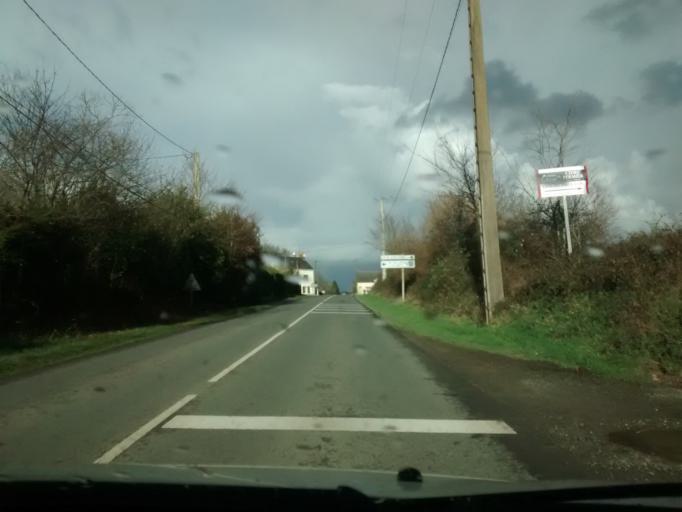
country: FR
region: Brittany
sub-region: Departement d'Ille-et-Vilaine
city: Liffre
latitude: 48.1863
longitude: -1.5146
